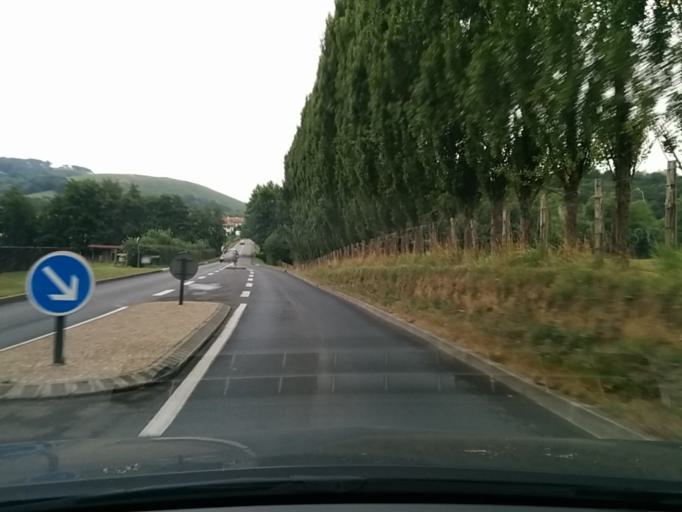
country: FR
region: Aquitaine
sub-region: Departement des Pyrenees-Atlantiques
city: Saint-Pee-sur-Nivelle
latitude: 43.3388
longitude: -1.5504
